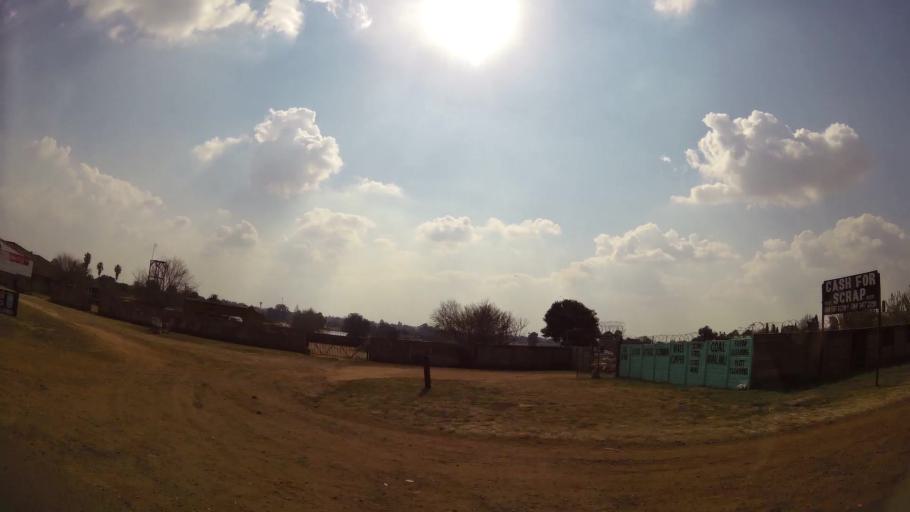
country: ZA
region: Mpumalanga
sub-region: Nkangala District Municipality
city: Delmas
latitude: -26.1871
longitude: 28.5415
